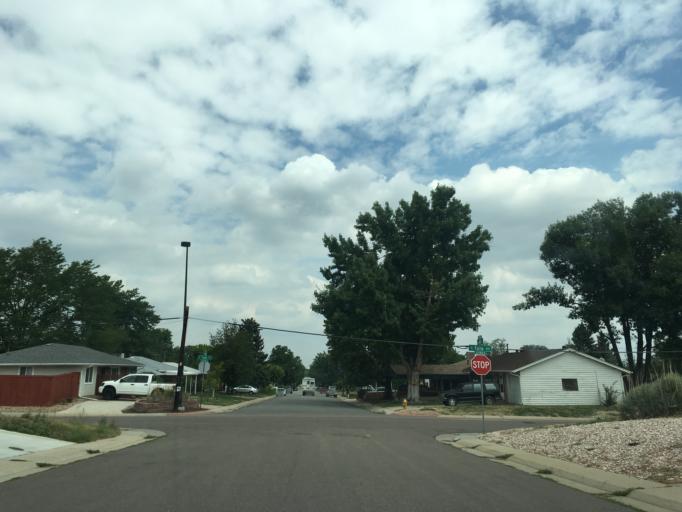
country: US
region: Colorado
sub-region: Arapahoe County
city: Sheridan
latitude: 39.6674
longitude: -105.0359
